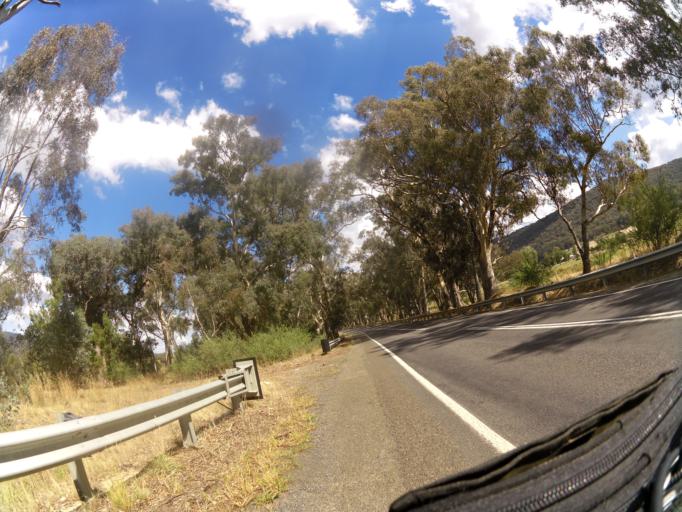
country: AU
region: Victoria
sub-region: Benalla
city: Benalla
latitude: -36.8046
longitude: 146.0076
